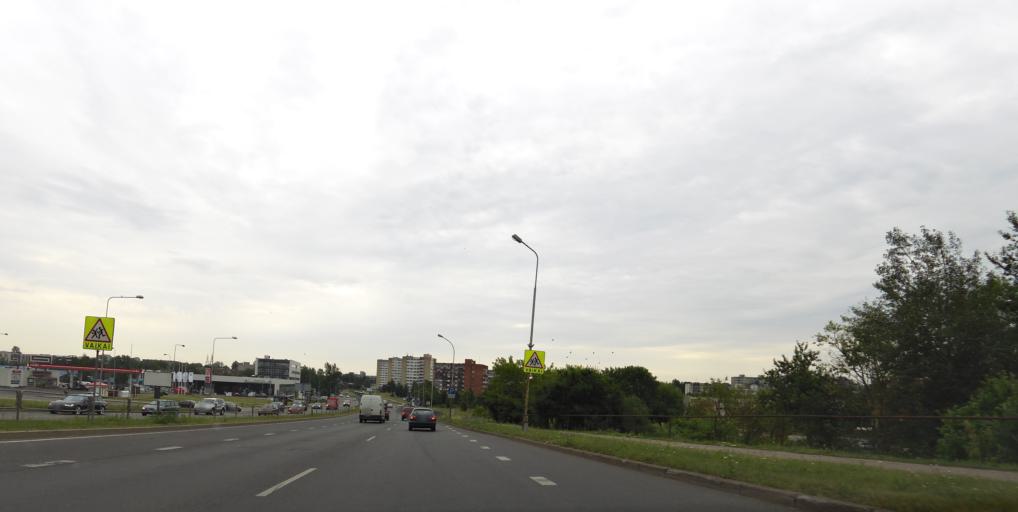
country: LT
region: Vilnius County
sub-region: Vilnius
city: Vilnius
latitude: 54.7127
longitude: 25.2754
